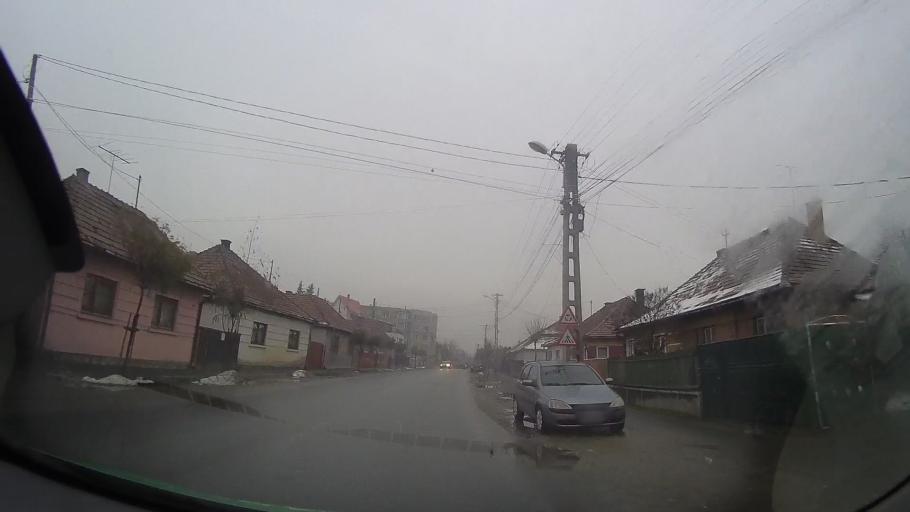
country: RO
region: Harghita
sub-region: Municipiul Gheorgheni
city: Gheorgheni
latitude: 46.7232
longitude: 25.5897
